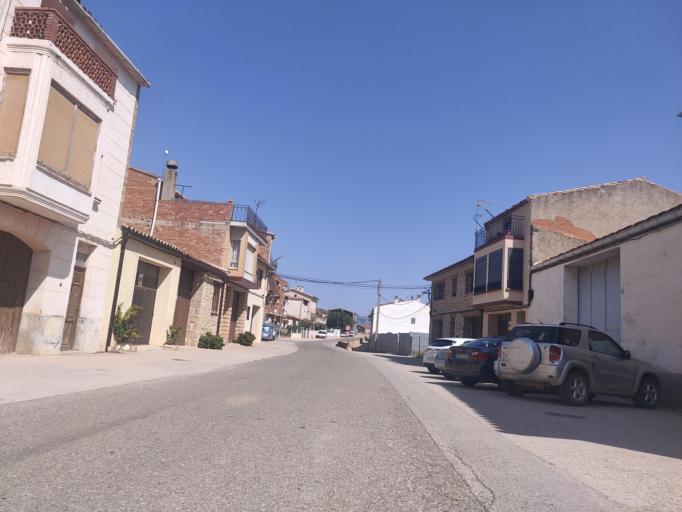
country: ES
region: Aragon
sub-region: Provincia de Teruel
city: Lledo
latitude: 40.9284
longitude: 0.2139
